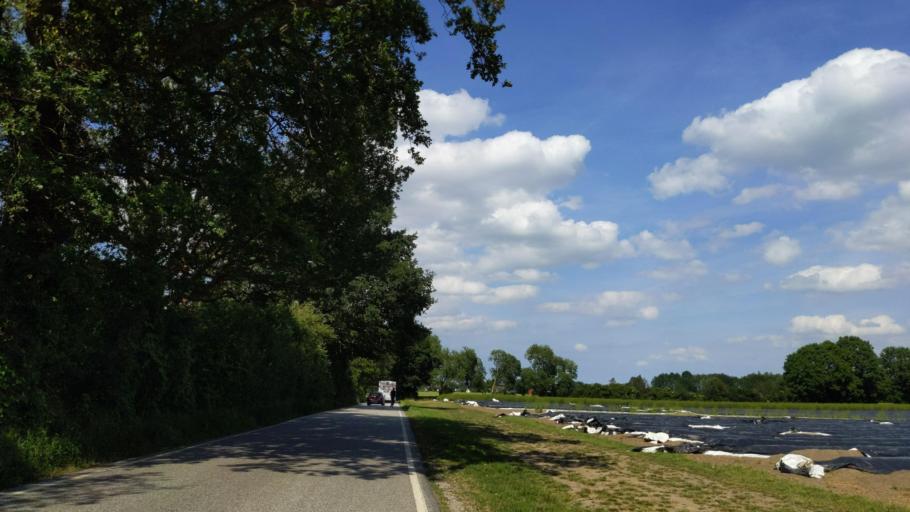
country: DE
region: Schleswig-Holstein
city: Krummesse
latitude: 53.8035
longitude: 10.6772
